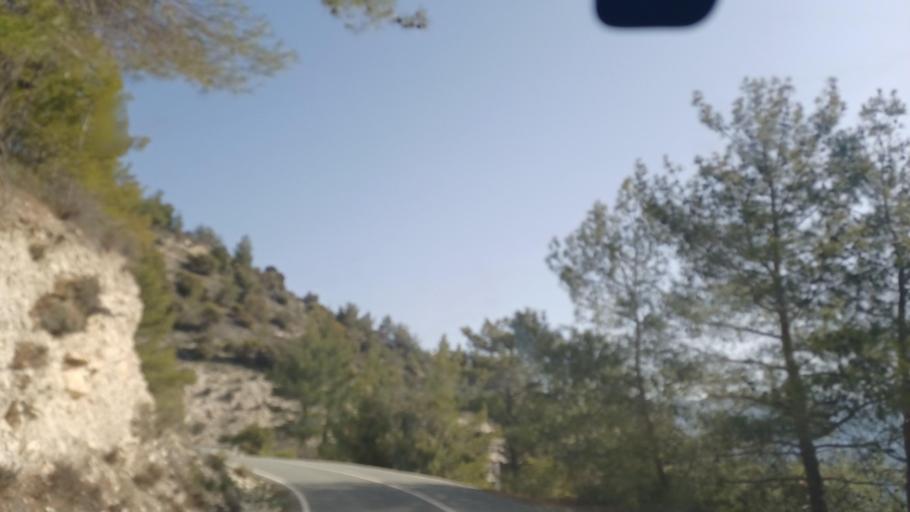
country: CY
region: Limassol
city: Pachna
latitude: 34.8808
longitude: 32.7309
